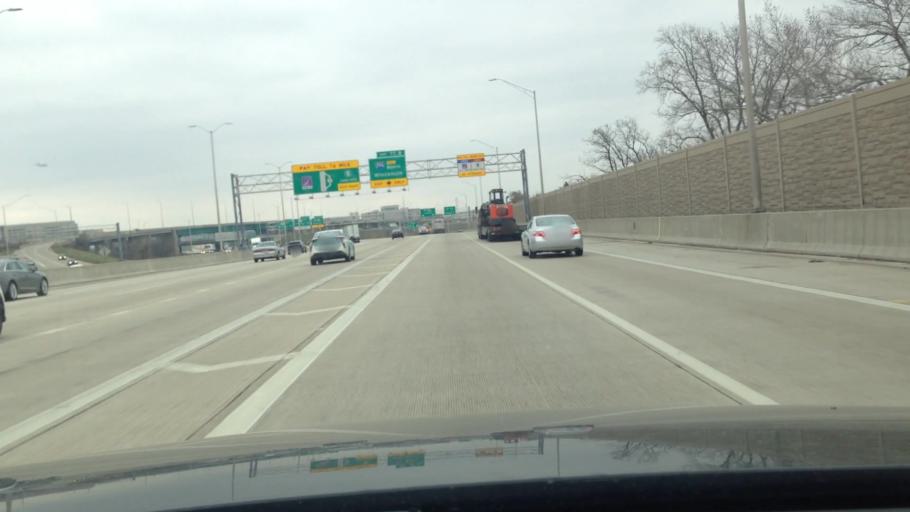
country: US
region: Illinois
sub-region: Cook County
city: Rosemont
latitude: 41.9939
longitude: -87.8731
